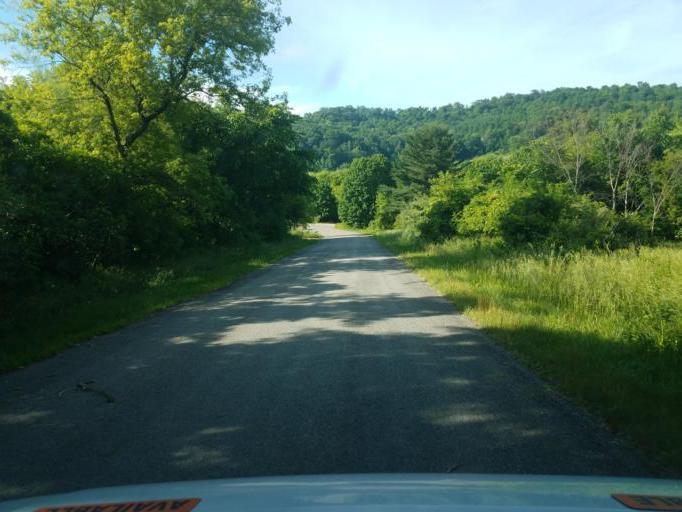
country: US
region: Wisconsin
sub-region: Vernon County
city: Hillsboro
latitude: 43.5851
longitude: -90.1776
